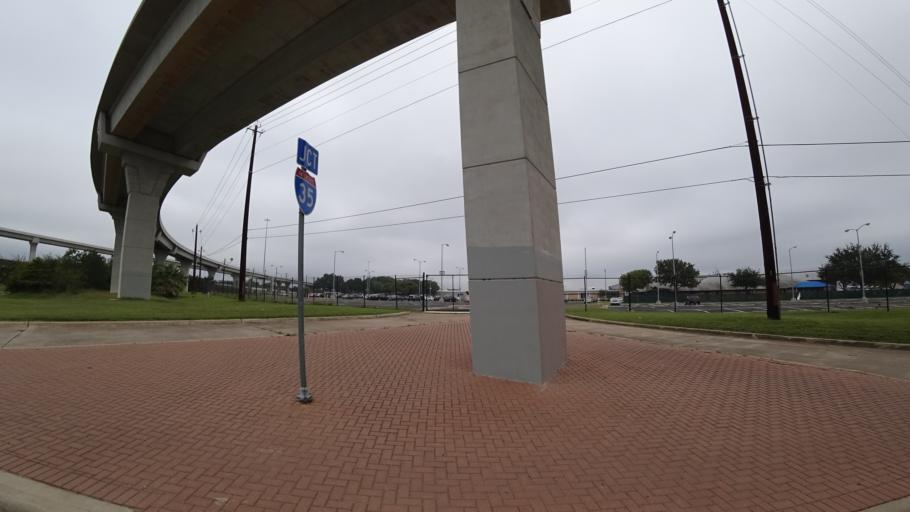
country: US
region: Texas
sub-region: Travis County
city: Austin
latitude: 30.2169
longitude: -97.7481
